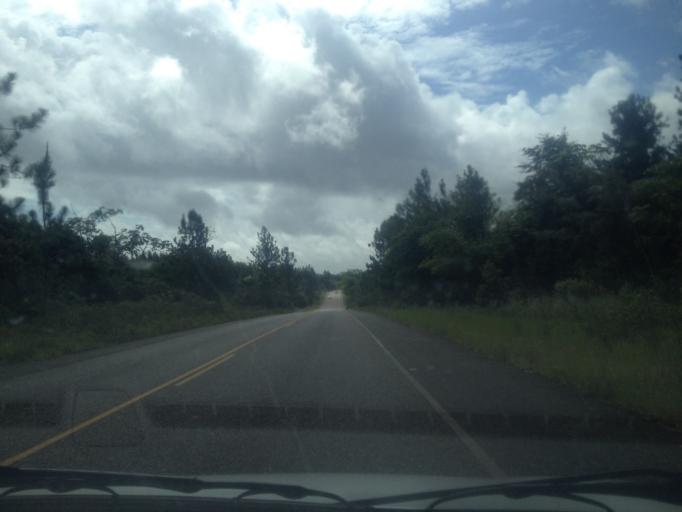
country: BR
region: Bahia
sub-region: Entre Rios
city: Entre Rios
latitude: -12.1582
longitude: -37.8044
